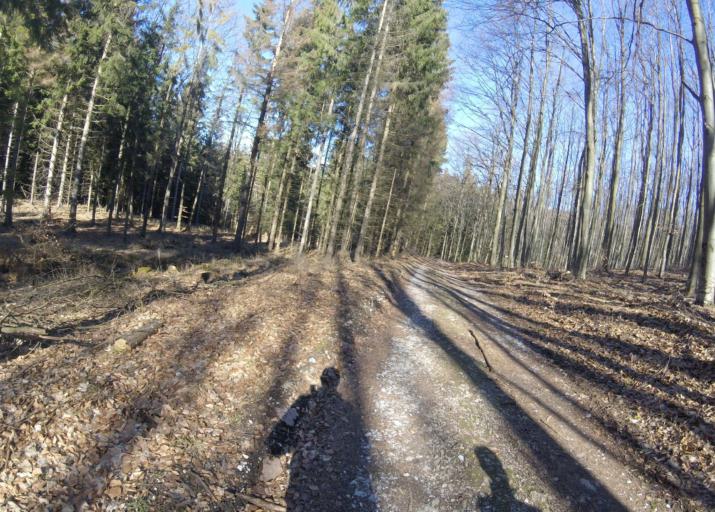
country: HU
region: Heves
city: Szilvasvarad
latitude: 48.0784
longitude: 20.4567
